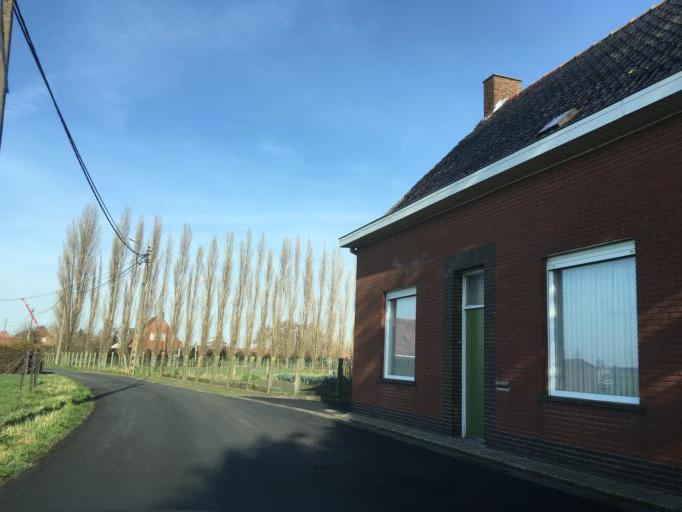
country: BE
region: Flanders
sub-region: Provincie West-Vlaanderen
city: Ardooie
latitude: 50.9528
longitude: 3.1716
